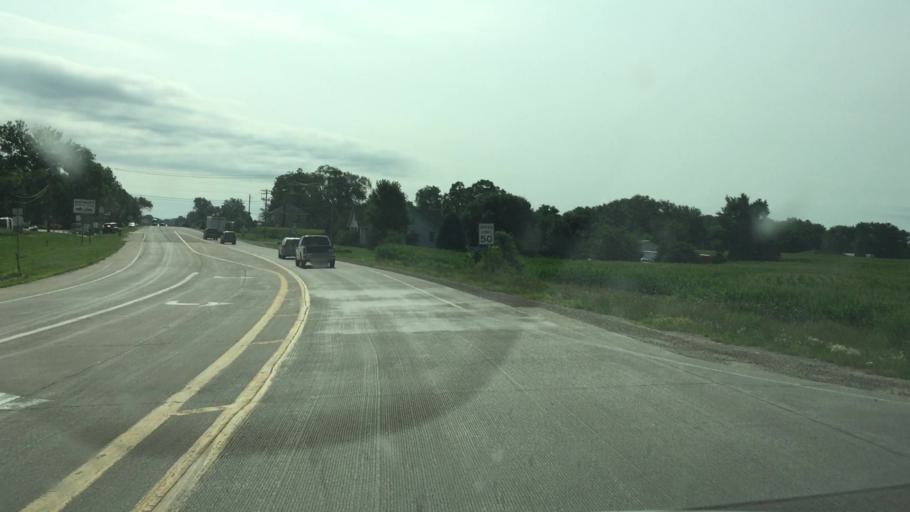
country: US
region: Illinois
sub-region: Hancock County
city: Nauvoo
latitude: 40.6244
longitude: -91.3953
